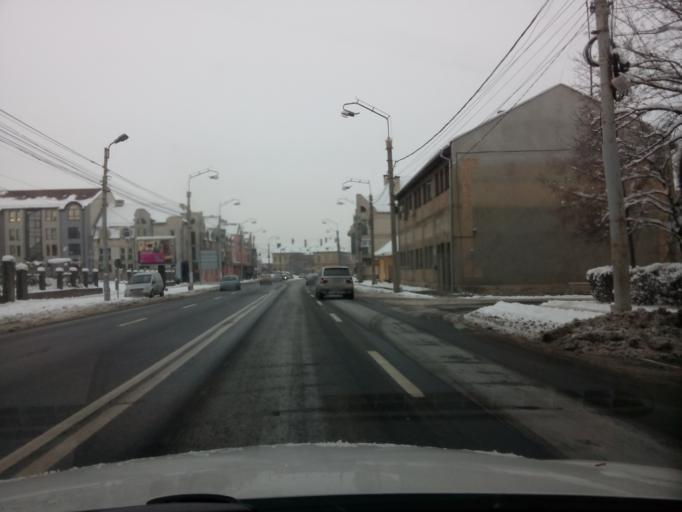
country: RO
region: Sibiu
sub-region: Municipiul Sibiu
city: Sibiu
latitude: 45.7976
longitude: 24.1583
